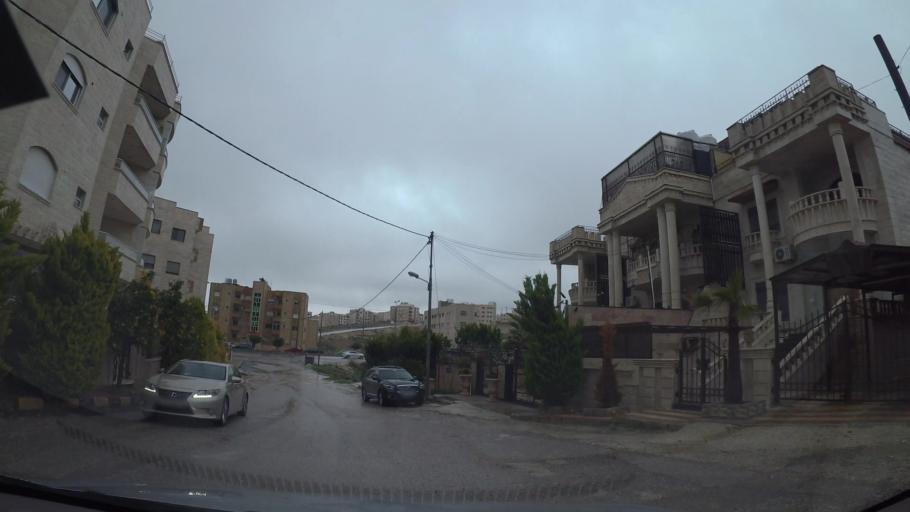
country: JO
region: Amman
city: Al Jubayhah
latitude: 32.0370
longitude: 35.8952
